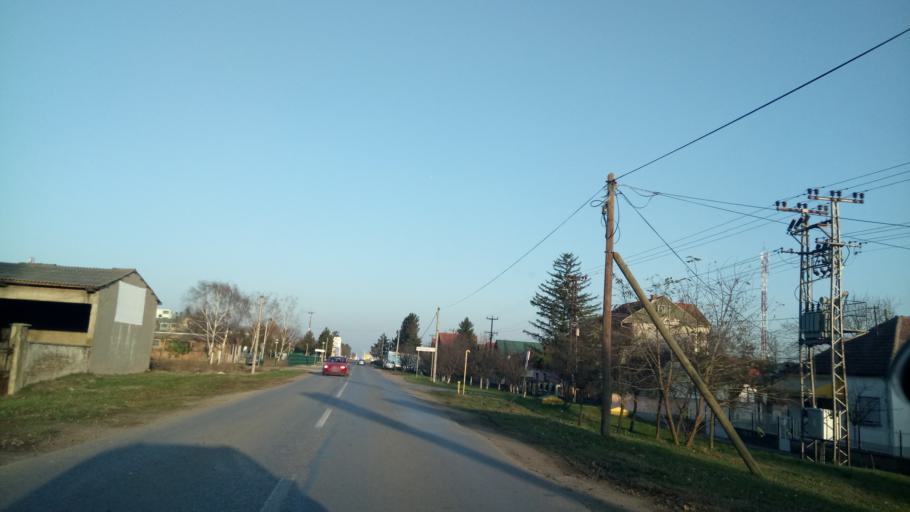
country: RS
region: Autonomna Pokrajina Vojvodina
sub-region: Sremski Okrug
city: Ingija
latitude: 45.0526
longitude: 20.0950
